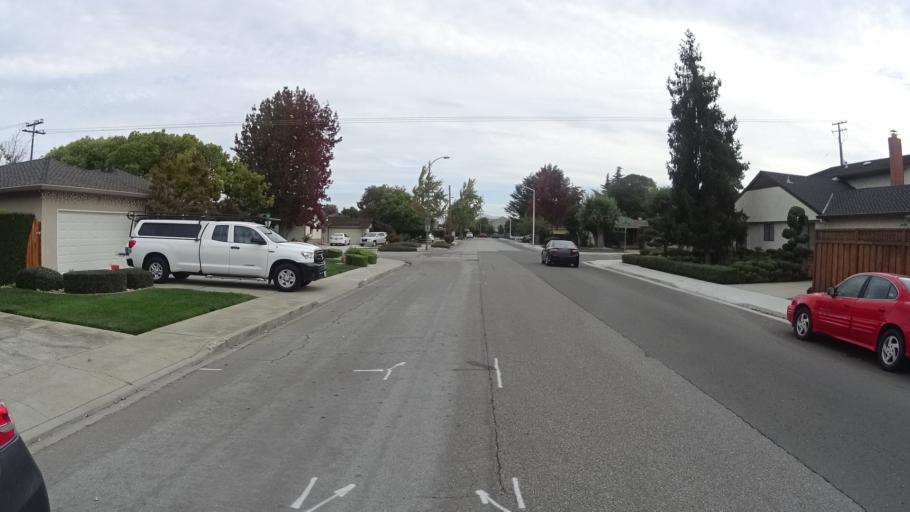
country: US
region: California
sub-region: Santa Clara County
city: Burbank
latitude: 37.3270
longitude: -121.9569
